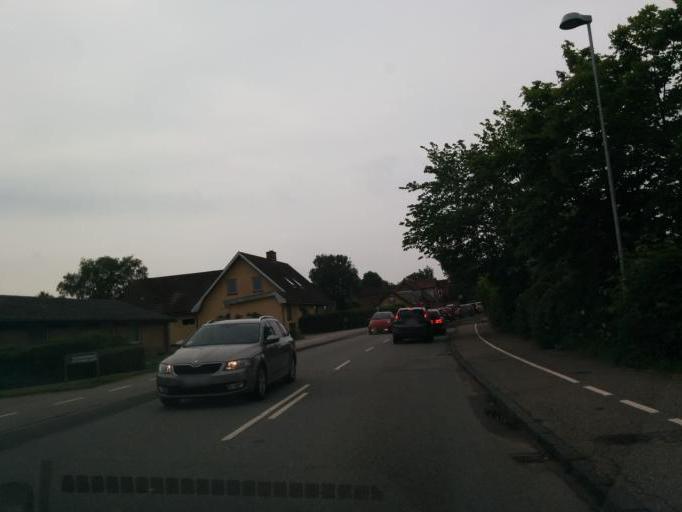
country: DK
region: Central Jutland
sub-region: Arhus Kommune
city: Logten
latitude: 56.2652
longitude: 10.3089
